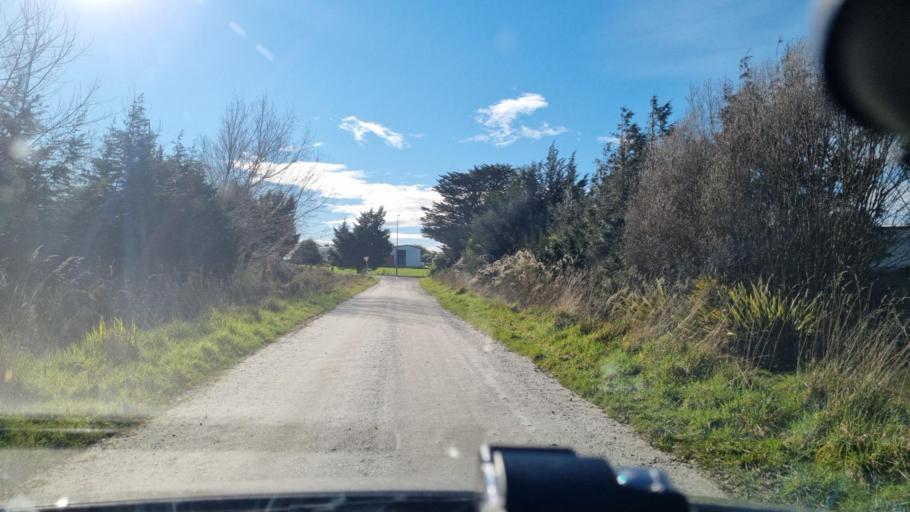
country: NZ
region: Southland
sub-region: Invercargill City
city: Invercargill
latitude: -46.4334
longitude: 168.3896
